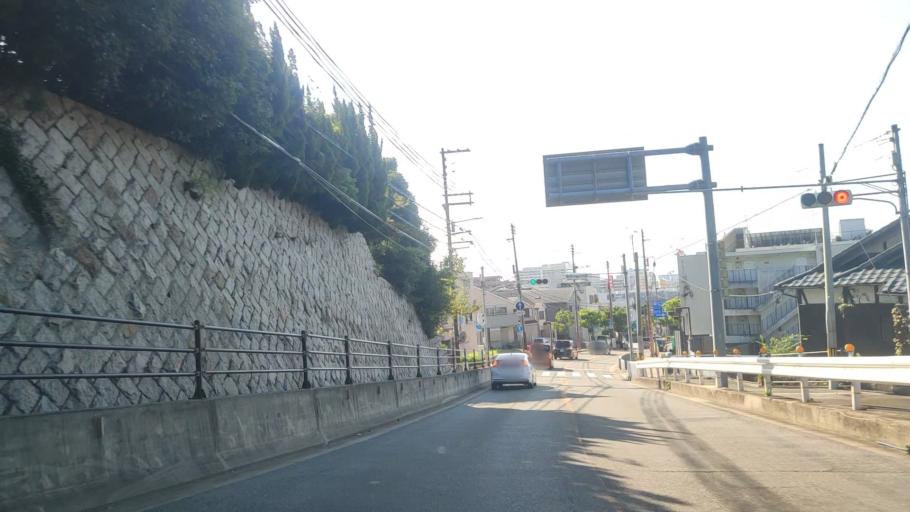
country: JP
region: Hyogo
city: Kobe
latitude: 34.6929
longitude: 135.1667
